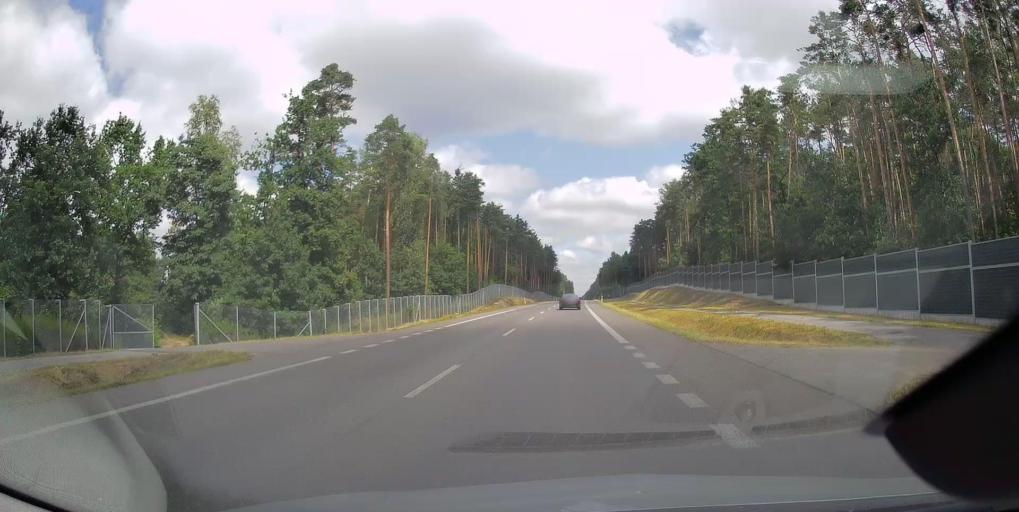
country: PL
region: Subcarpathian Voivodeship
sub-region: Powiat mielecki
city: Przeclaw
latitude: 50.2629
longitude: 21.4933
